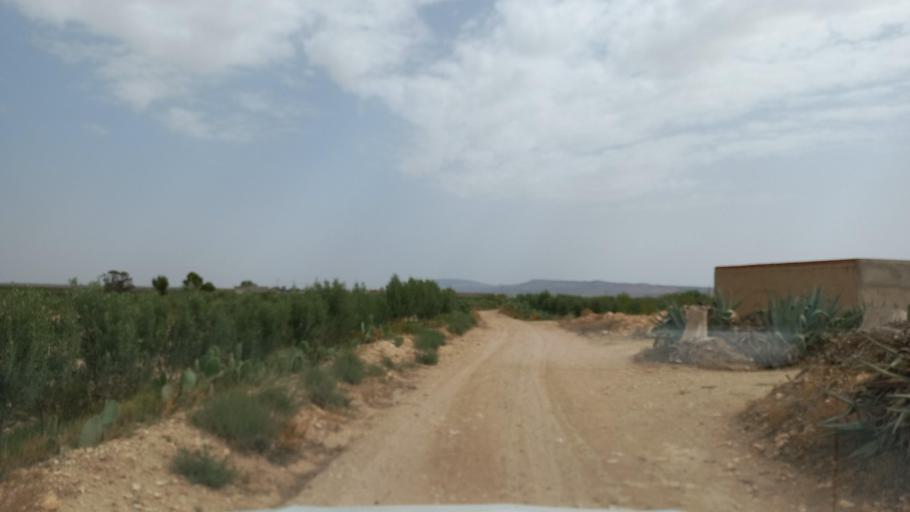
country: TN
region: Al Qasrayn
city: Kasserine
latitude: 35.2822
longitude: 9.0192
